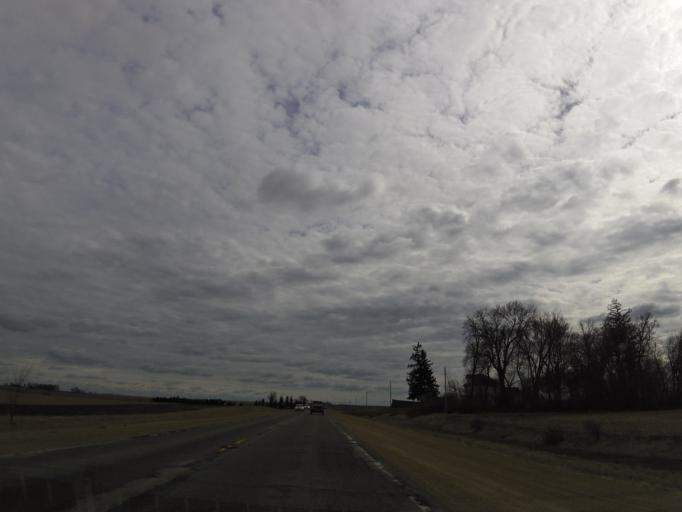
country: US
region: Iowa
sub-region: Howard County
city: Cresco
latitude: 43.3420
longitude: -92.2986
